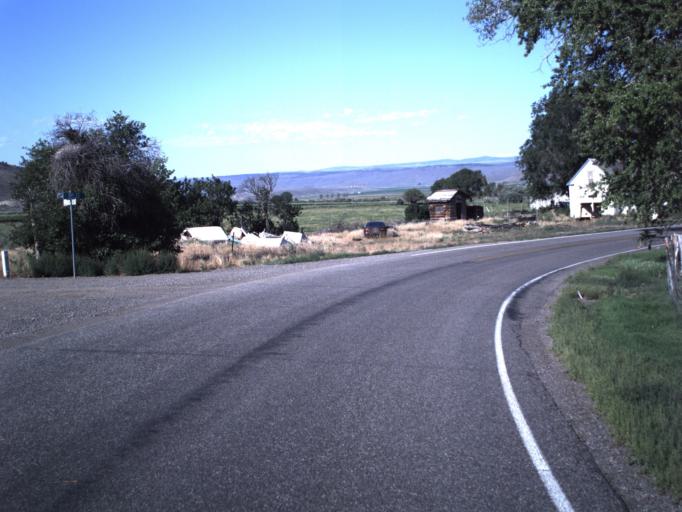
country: US
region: Utah
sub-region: Wayne County
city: Loa
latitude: 38.4624
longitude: -111.5962
